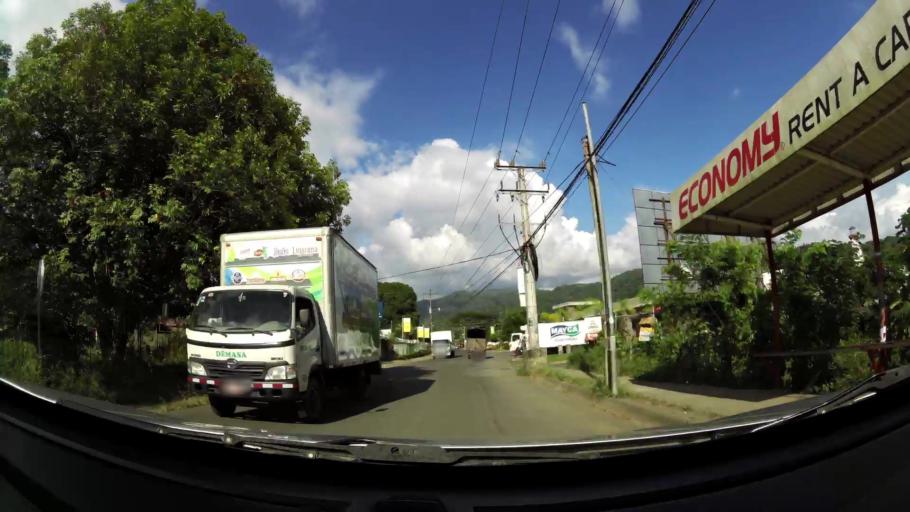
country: CR
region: Puntarenas
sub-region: Canton de Garabito
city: Jaco
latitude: 9.6612
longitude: -84.6400
